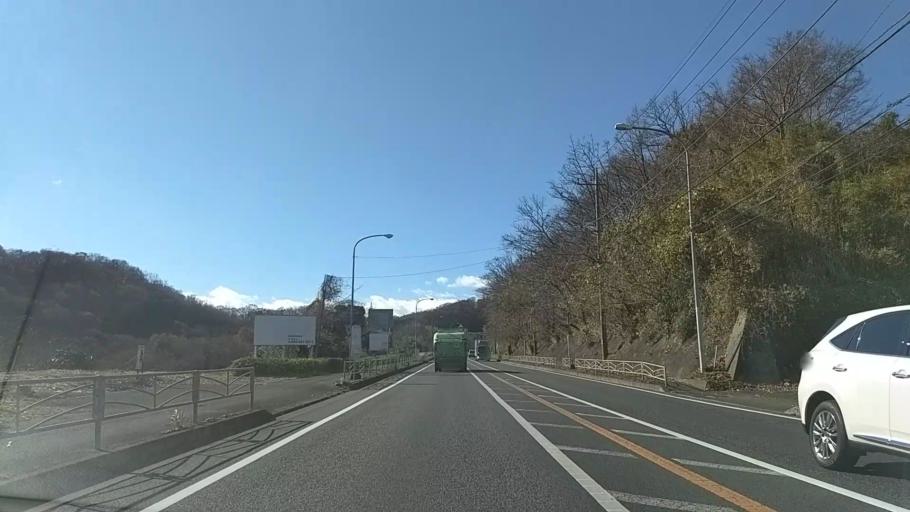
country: JP
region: Kanagawa
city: Hadano
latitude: 35.3862
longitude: 139.2588
